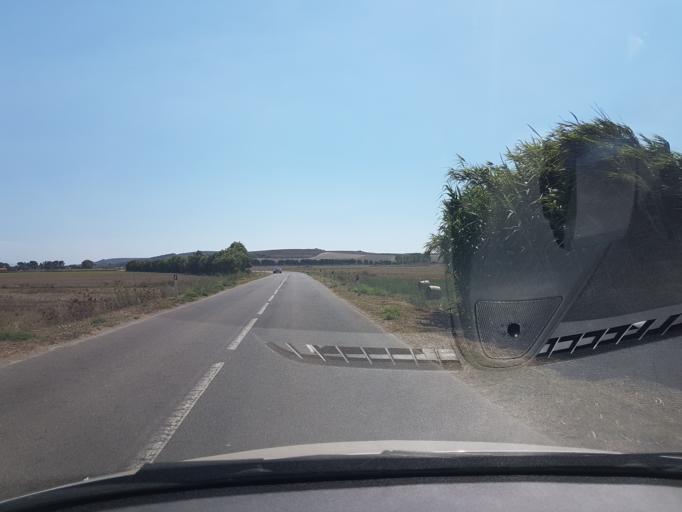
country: IT
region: Sardinia
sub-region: Provincia di Oristano
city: Nurachi
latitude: 39.9751
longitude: 8.4529
